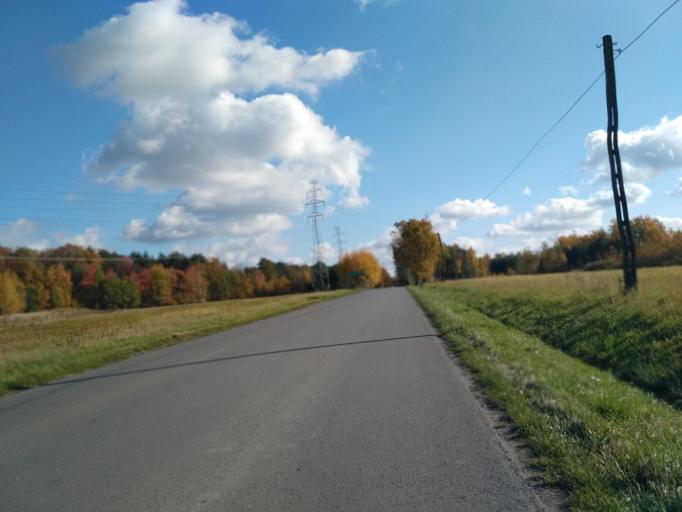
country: PL
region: Subcarpathian Voivodeship
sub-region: Powiat rzeszowski
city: Glogow Malopolski
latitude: 50.1568
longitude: 21.9207
